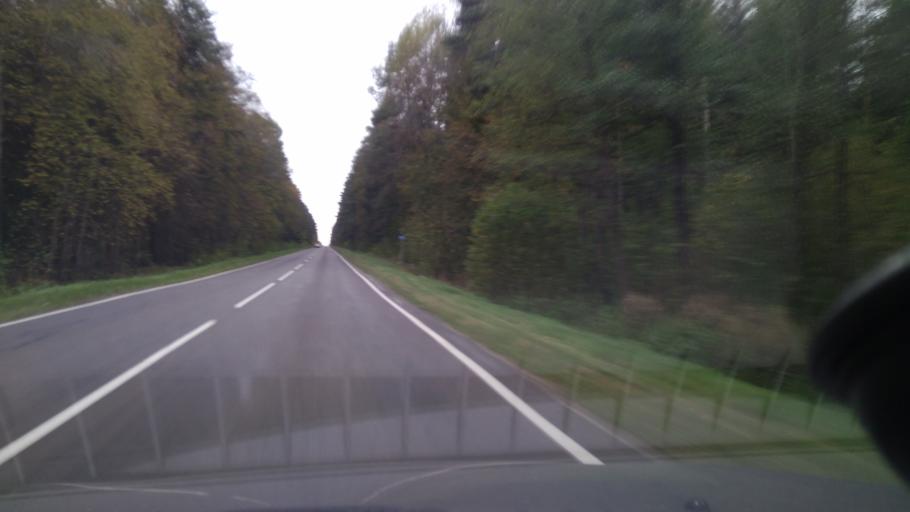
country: BY
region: Minsk
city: Druzhny
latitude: 53.6313
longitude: 27.8847
